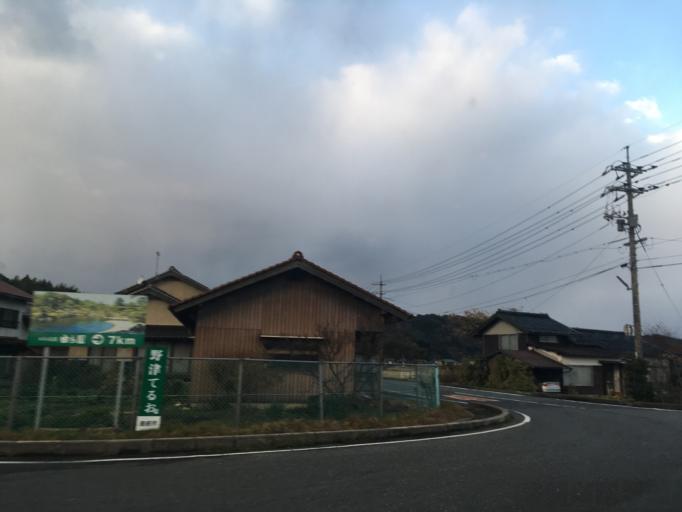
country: JP
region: Shimane
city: Matsue-shi
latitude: 35.4577
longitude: 133.1236
